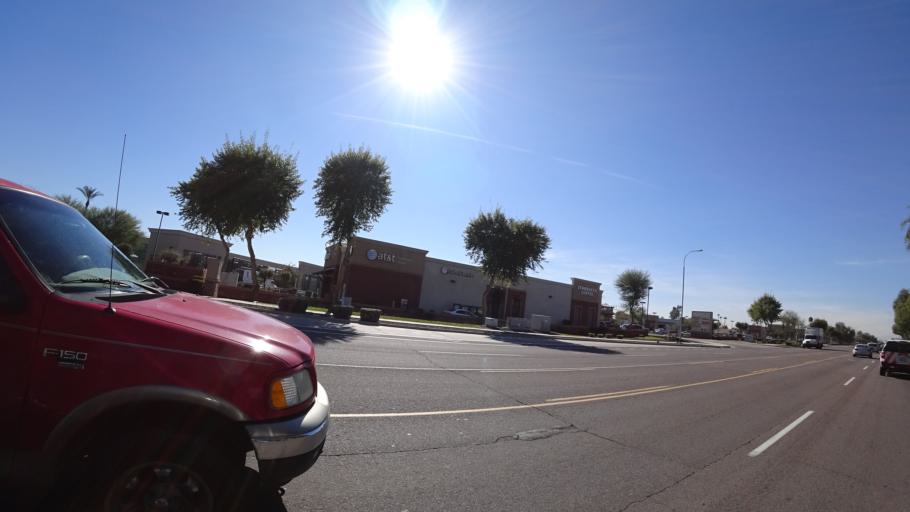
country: US
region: Arizona
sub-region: Maricopa County
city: Tolleson
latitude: 33.5084
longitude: -112.2752
